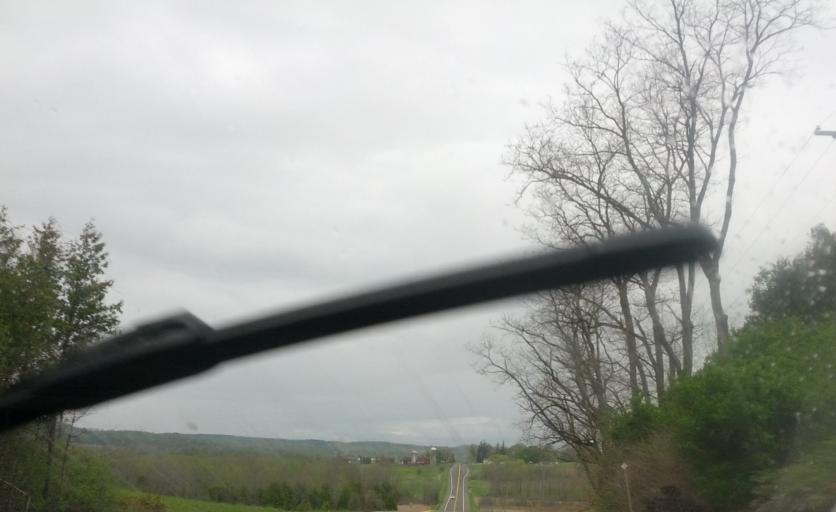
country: US
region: New York
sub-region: Madison County
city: Cazenovia
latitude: 42.9238
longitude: -75.9371
